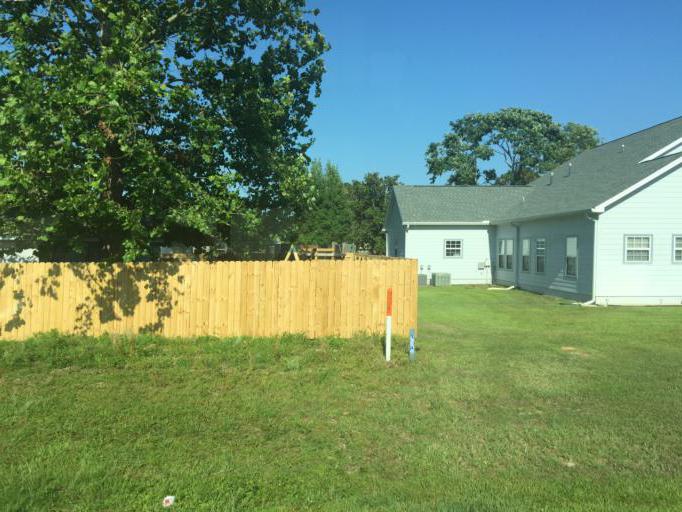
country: US
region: Florida
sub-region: Bay County
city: Panama City Beach
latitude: 30.2026
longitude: -85.8359
